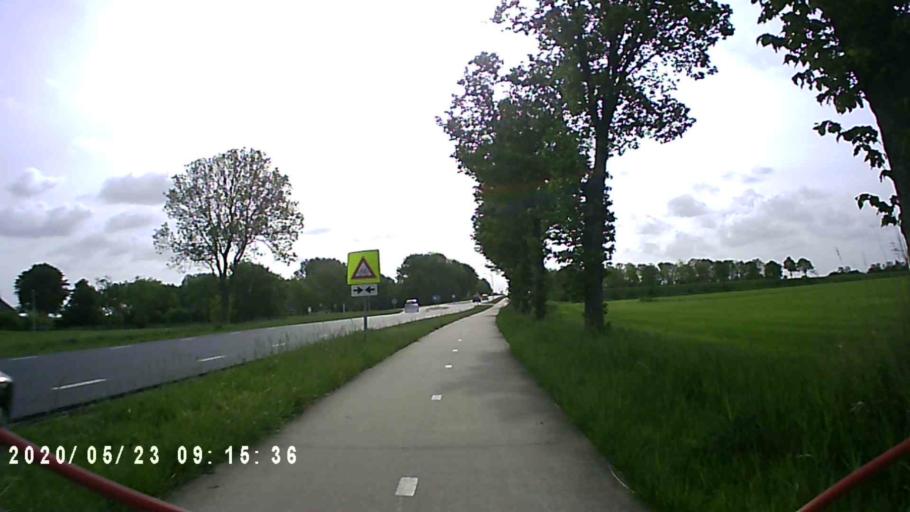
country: NL
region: Groningen
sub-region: Gemeente Bedum
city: Bedum
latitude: 53.3023
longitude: 6.6451
